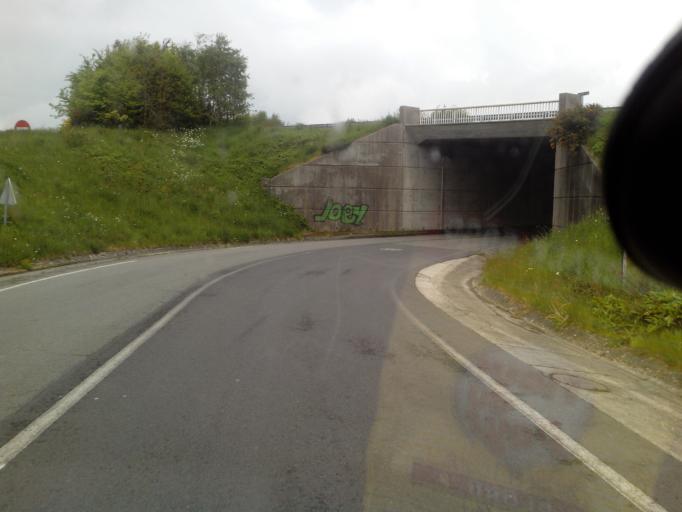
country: FR
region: Lower Normandy
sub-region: Departement de la Manche
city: Tessy-sur-Vire
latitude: 48.9070
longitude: -1.1056
